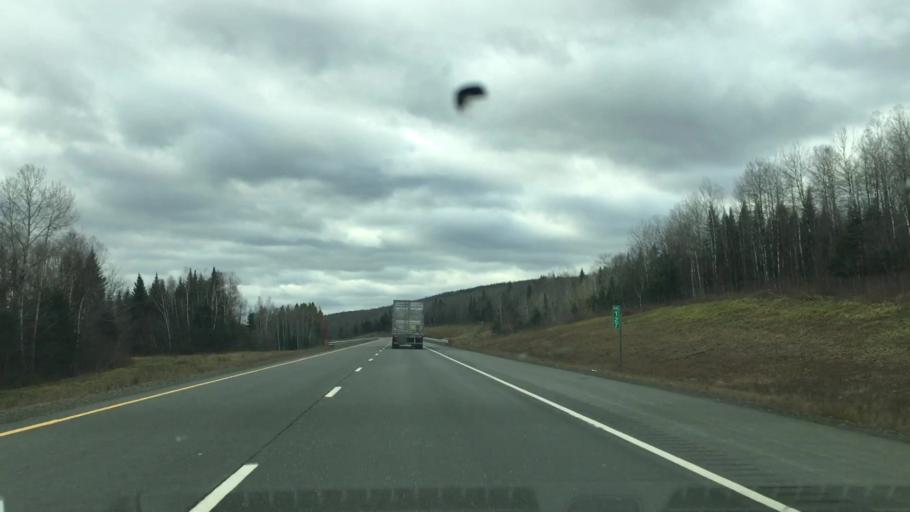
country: US
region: Maine
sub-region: Aroostook County
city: Fort Fairfield
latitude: 46.6549
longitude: -67.7373
